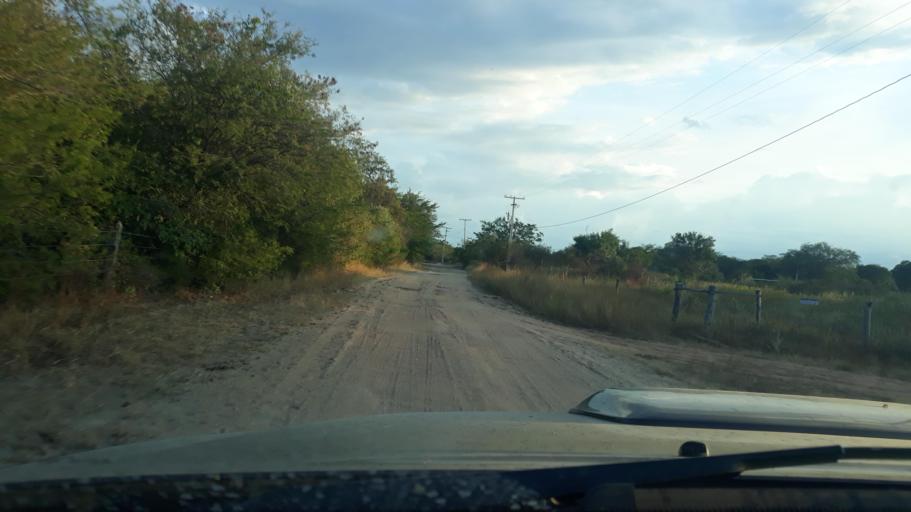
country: BR
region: Bahia
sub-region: Riacho De Santana
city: Riacho de Santana
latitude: -13.8742
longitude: -43.0202
